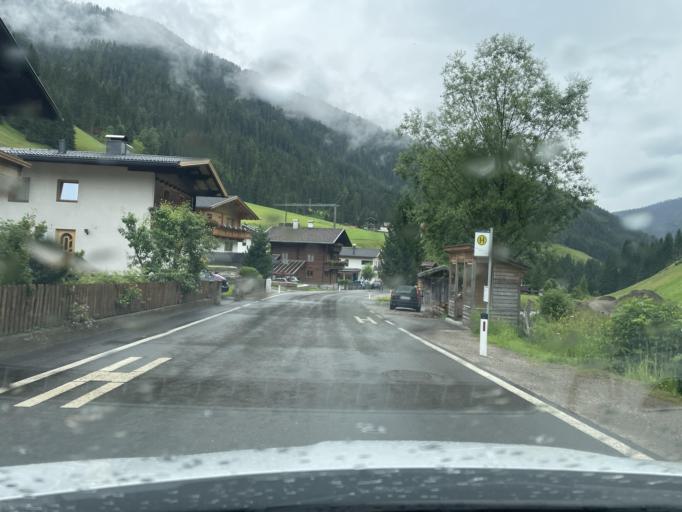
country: AT
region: Tyrol
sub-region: Politischer Bezirk Lienz
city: Ausservillgraten
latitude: 46.7969
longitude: 12.4465
